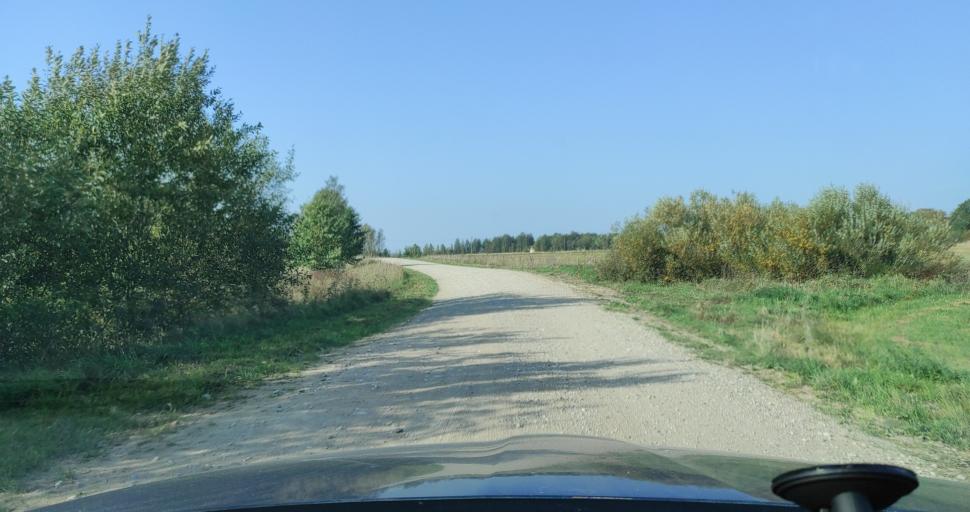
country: LV
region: Ventspils Rajons
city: Piltene
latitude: 57.2240
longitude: 21.6222
